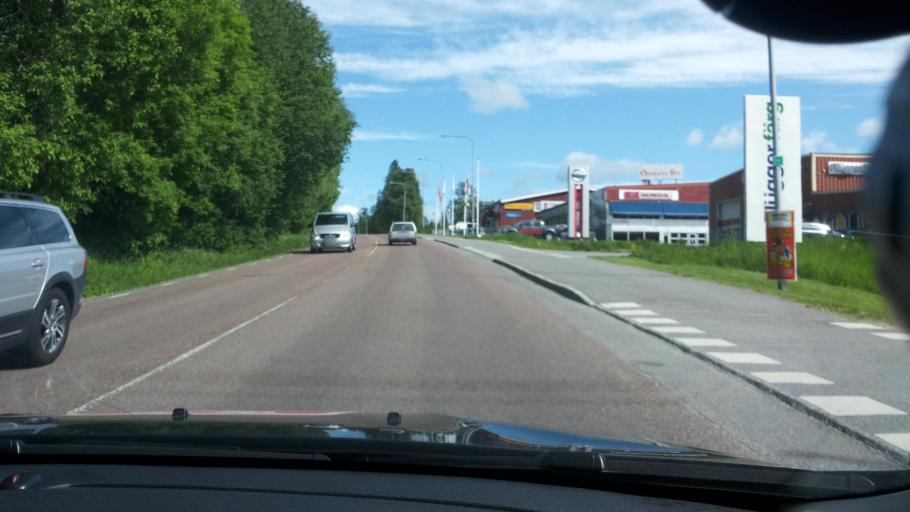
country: SE
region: Vaesternorrland
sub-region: Sundsvalls Kommun
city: Johannedal
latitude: 62.4247
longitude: 17.3466
